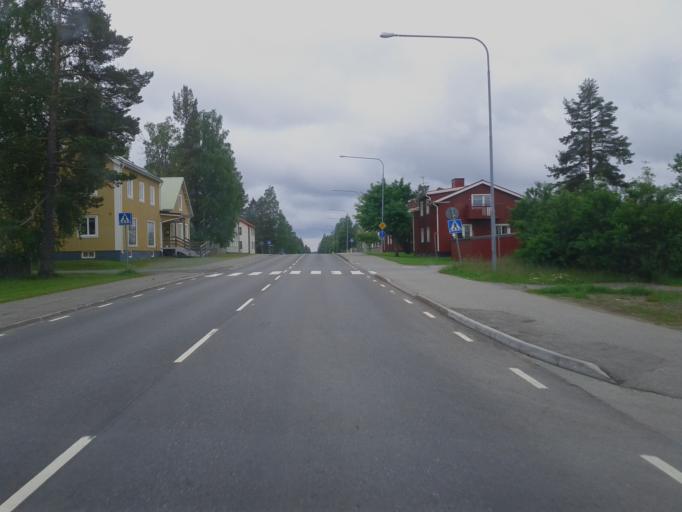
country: SE
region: Vaesterbotten
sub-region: Skelleftea Kommun
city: Boliden
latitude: 64.8664
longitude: 20.3888
